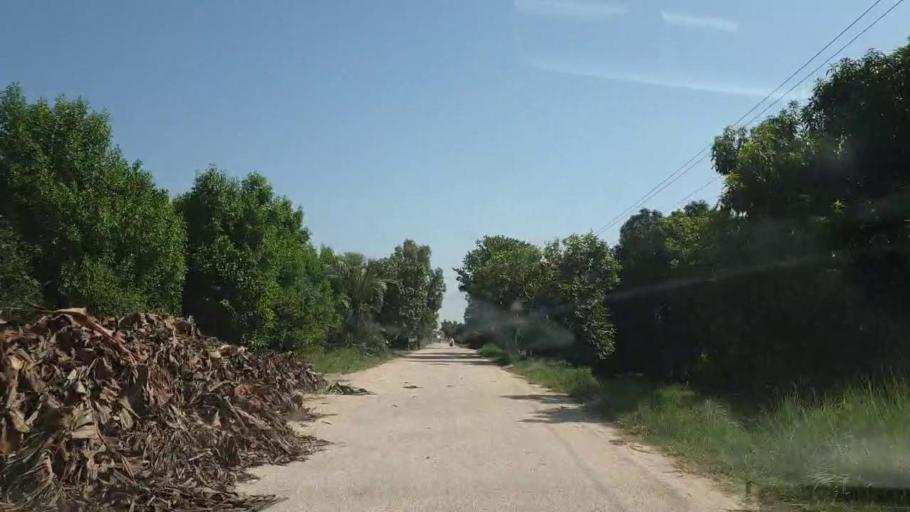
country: PK
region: Sindh
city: Tando Jam
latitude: 25.4046
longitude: 68.5833
